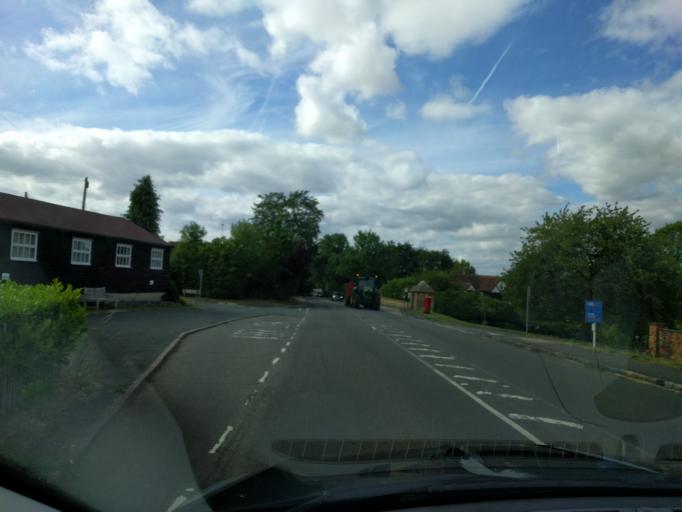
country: GB
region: England
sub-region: Warwickshire
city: Shipston on Stour
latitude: 52.0910
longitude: -1.6267
